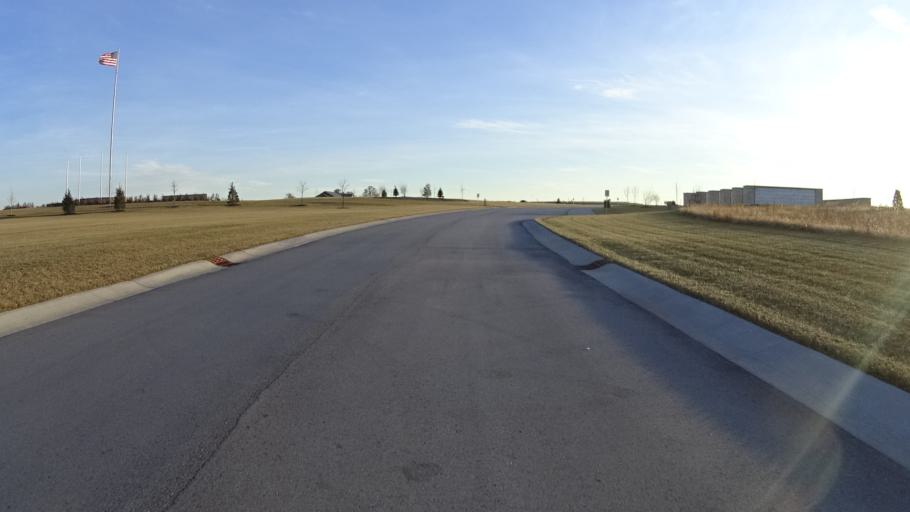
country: US
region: Nebraska
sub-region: Sarpy County
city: Chalco
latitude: 41.1379
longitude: -96.1339
